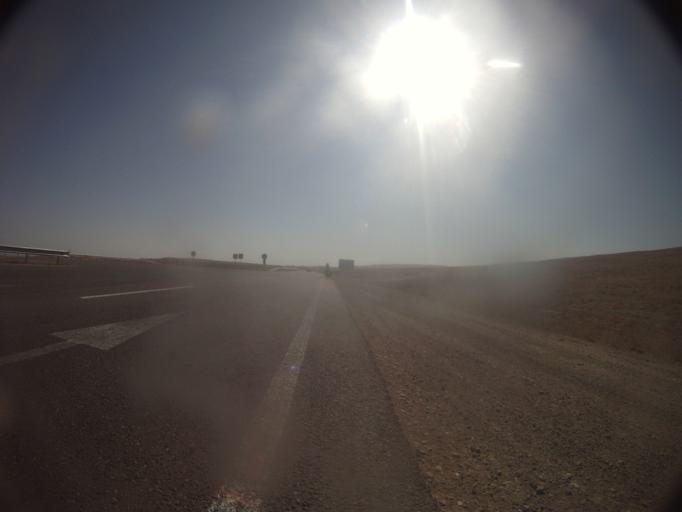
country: KZ
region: Zhambyl
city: Taraz
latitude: 42.7319
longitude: 70.9062
